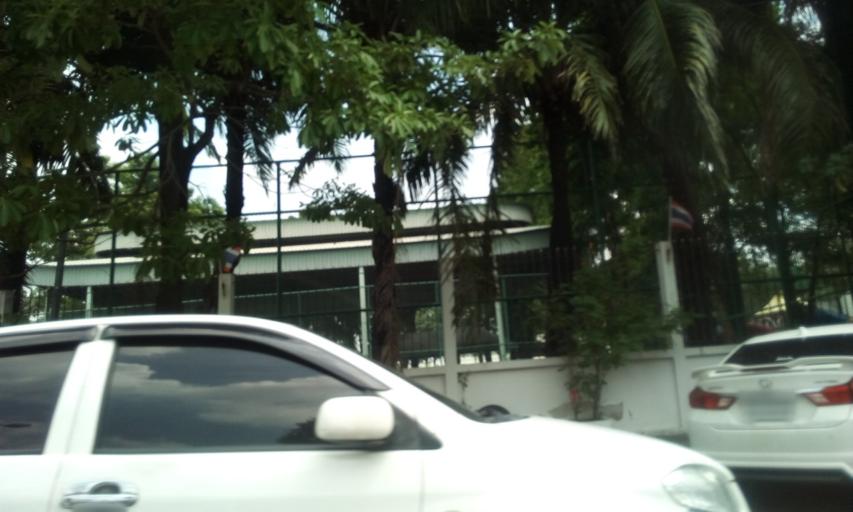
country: TH
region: Bangkok
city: Lak Si
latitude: 13.9122
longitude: 100.5550
